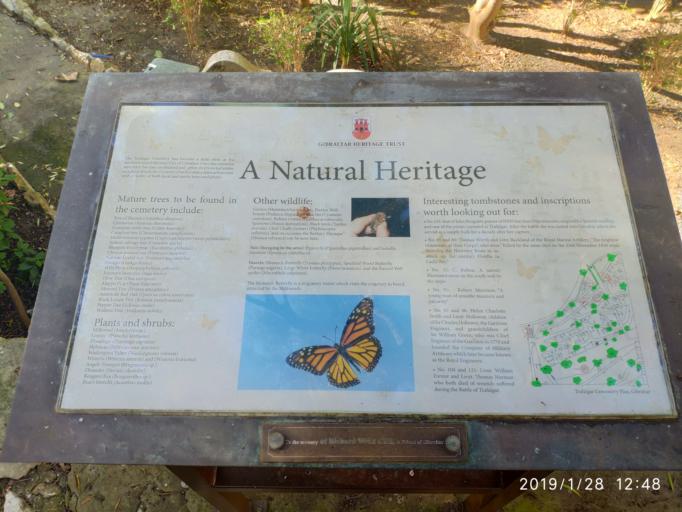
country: GI
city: Gibraltar
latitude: 36.1346
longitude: -5.3520
